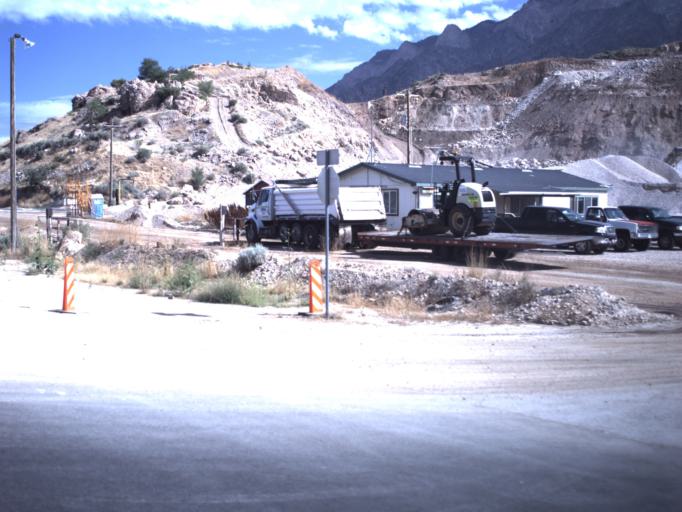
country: US
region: Utah
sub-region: Box Elder County
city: South Willard
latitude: 41.3401
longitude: -112.0306
